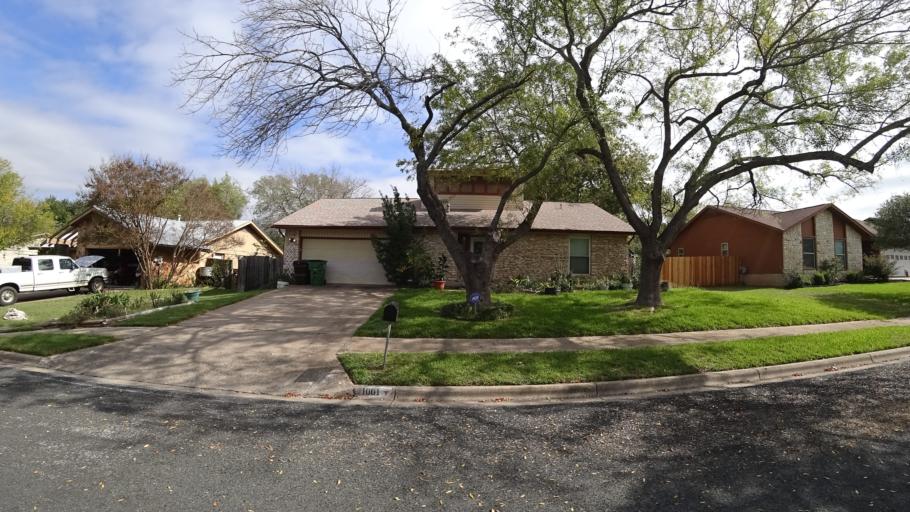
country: US
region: Texas
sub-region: Williamson County
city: Brushy Creek
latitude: 30.5178
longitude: -97.7345
